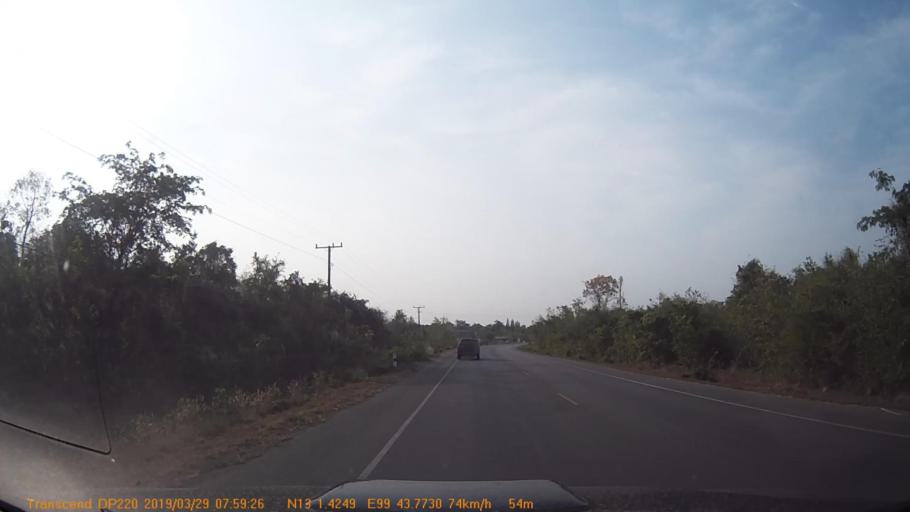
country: TH
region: Phetchaburi
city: Kaeng Krachan
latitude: 13.0235
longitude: 99.7297
